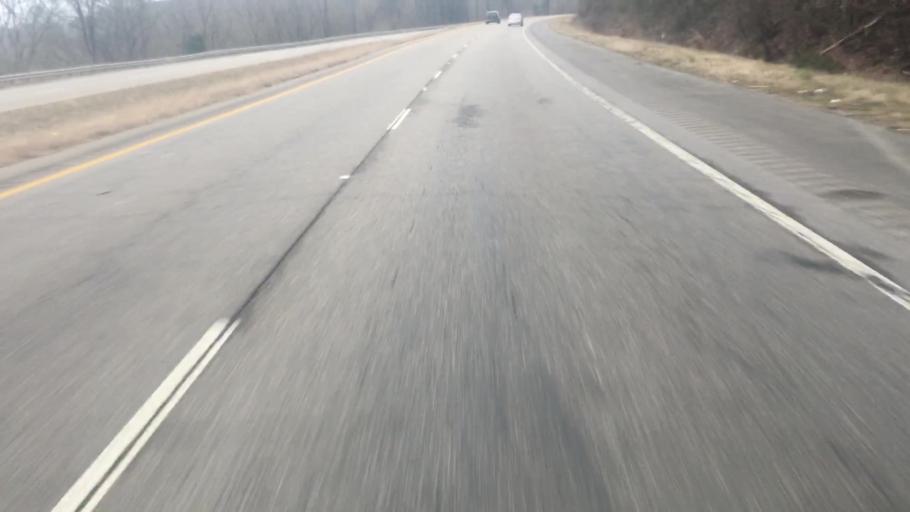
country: US
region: Alabama
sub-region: Walker County
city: Cordova
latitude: 33.8157
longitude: -87.1492
